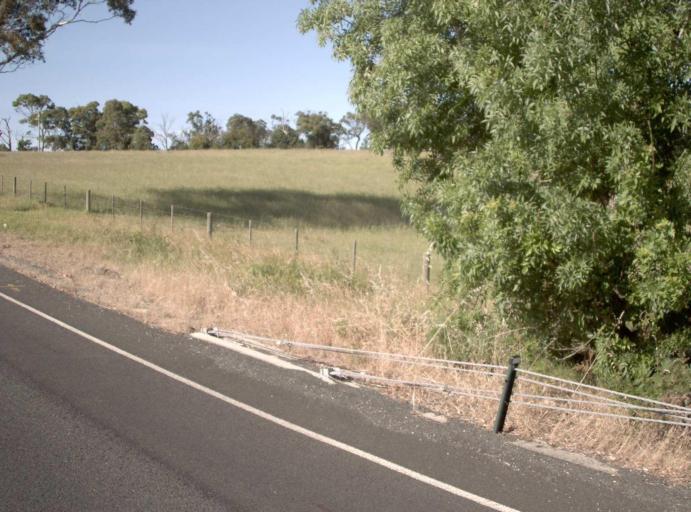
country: AU
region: Victoria
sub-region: East Gippsland
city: Lakes Entrance
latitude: -37.8559
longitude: 147.8452
